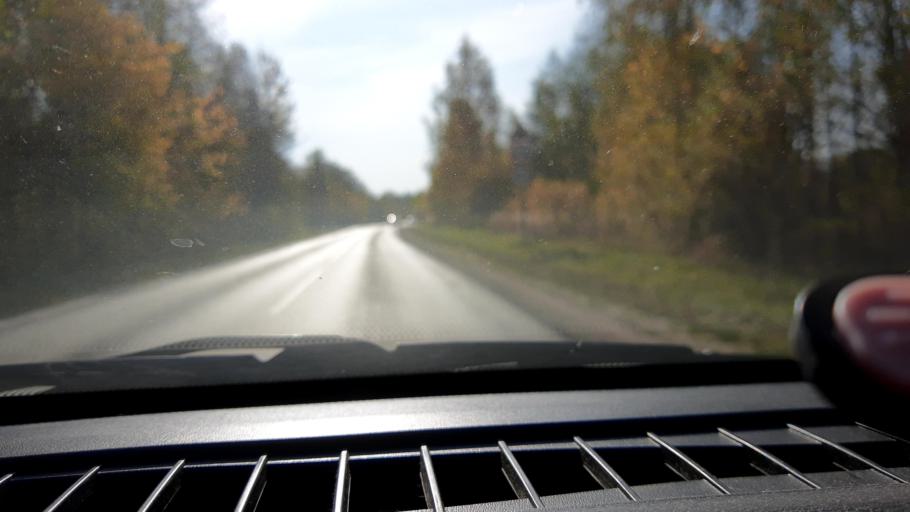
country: RU
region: Nizjnij Novgorod
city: Neklyudovo
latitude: 56.4300
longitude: 43.9232
